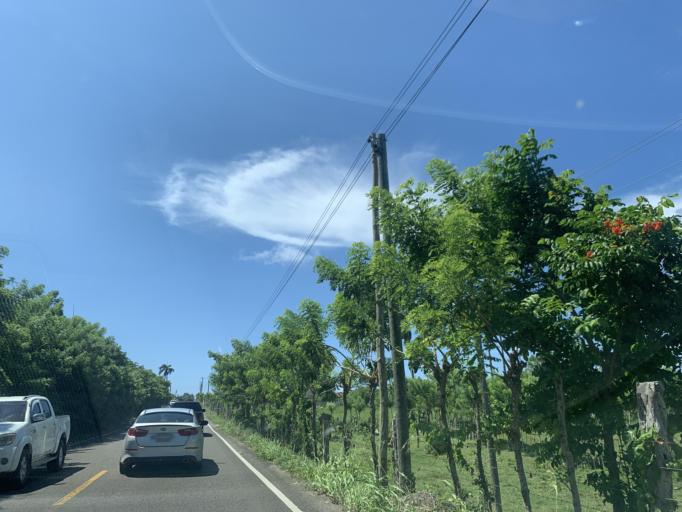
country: DO
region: Maria Trinidad Sanchez
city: Cabrera
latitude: 19.6686
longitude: -69.9510
